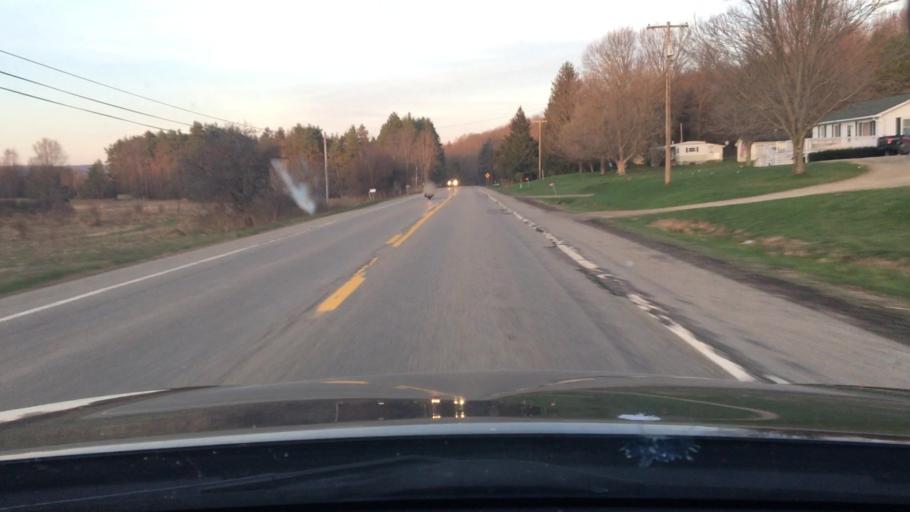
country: US
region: New York
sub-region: Cattaraugus County
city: Randolph
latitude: 42.1769
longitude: -78.9297
